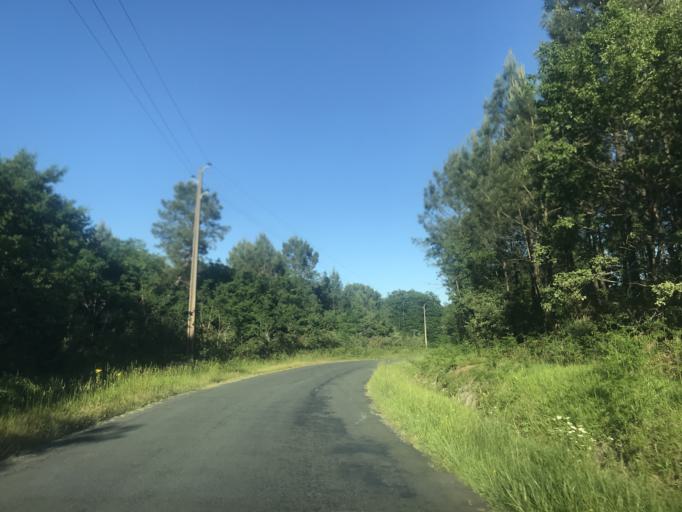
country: FR
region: Aquitaine
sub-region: Departement de la Gironde
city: Saint-Savin
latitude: 45.1135
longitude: -0.4578
